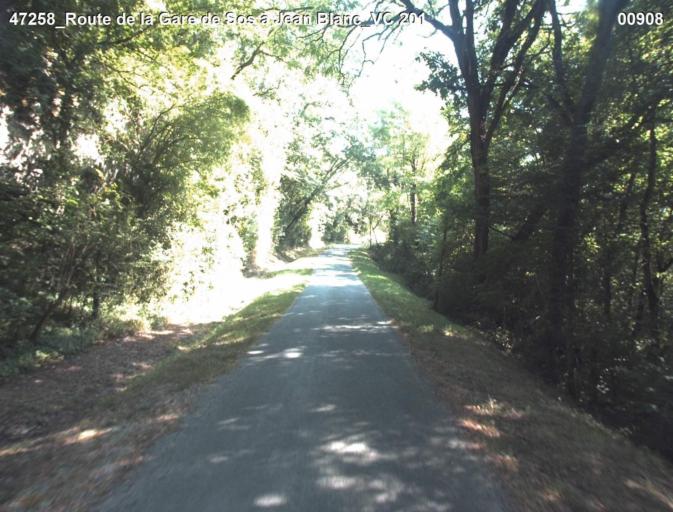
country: FR
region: Midi-Pyrenees
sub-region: Departement du Gers
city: Montreal
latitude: 44.0357
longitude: 0.1491
